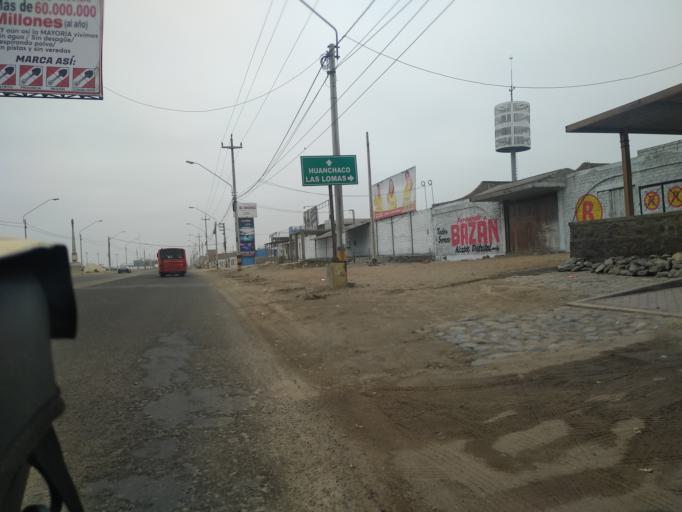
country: PE
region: La Libertad
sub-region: Provincia de Trujillo
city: Huanchaco
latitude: -8.0939
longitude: -79.1155
